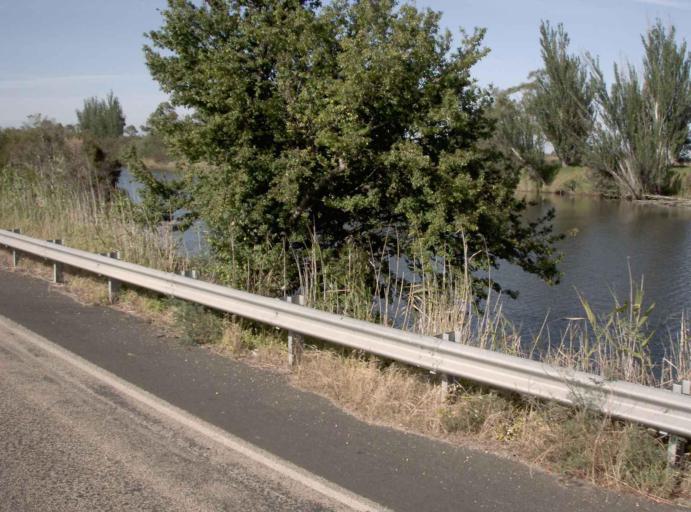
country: AU
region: Victoria
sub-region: East Gippsland
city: Lakes Entrance
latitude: -37.8328
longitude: 147.8626
